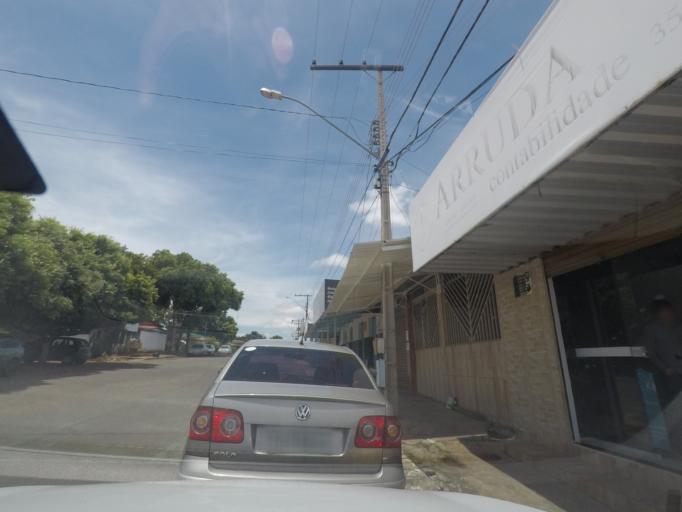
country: BR
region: Goias
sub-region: Goiania
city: Goiania
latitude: -16.6616
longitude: -49.1963
